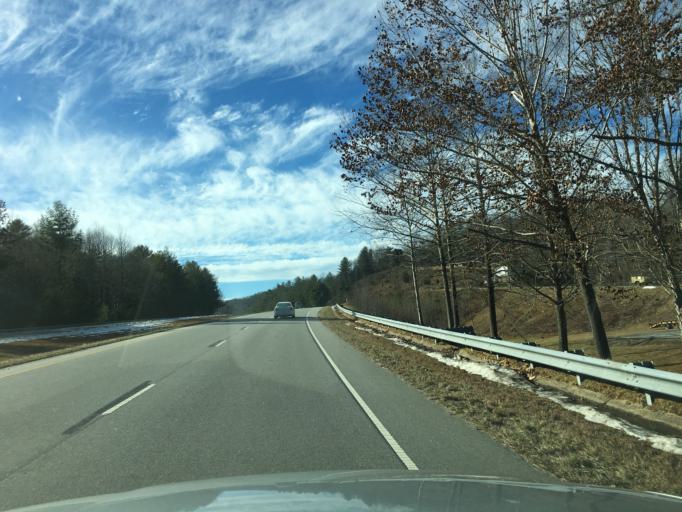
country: US
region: North Carolina
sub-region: Transylvania County
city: Brevard
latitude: 35.2020
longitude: -82.7728
